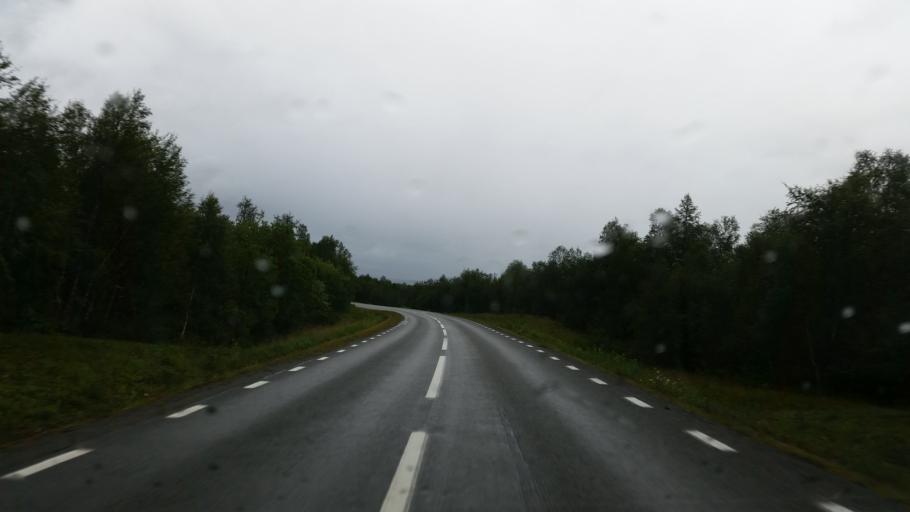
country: NO
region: Nordland
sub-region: Rana
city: Mo i Rana
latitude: 65.8844
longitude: 14.9881
